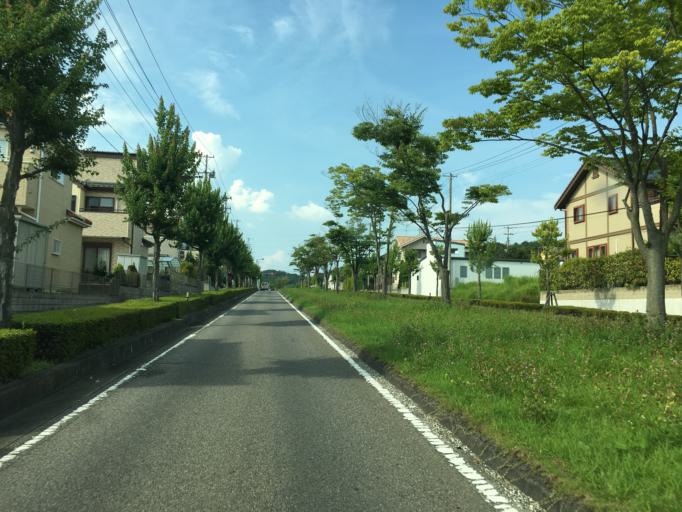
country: JP
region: Fukushima
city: Koriyama
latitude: 37.3845
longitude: 140.4351
